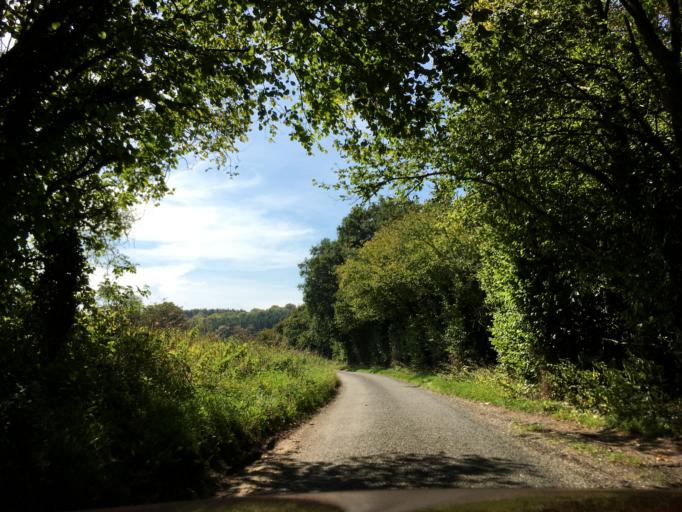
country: GB
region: England
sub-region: Hampshire
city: Highclere
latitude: 51.2824
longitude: -1.3594
